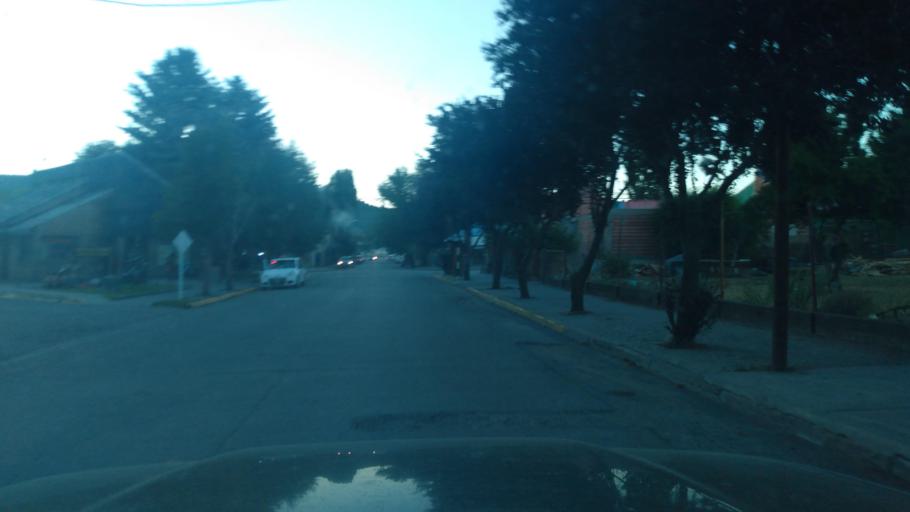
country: AR
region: Neuquen
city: Junin de los Andes
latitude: -39.9487
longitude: -71.0729
